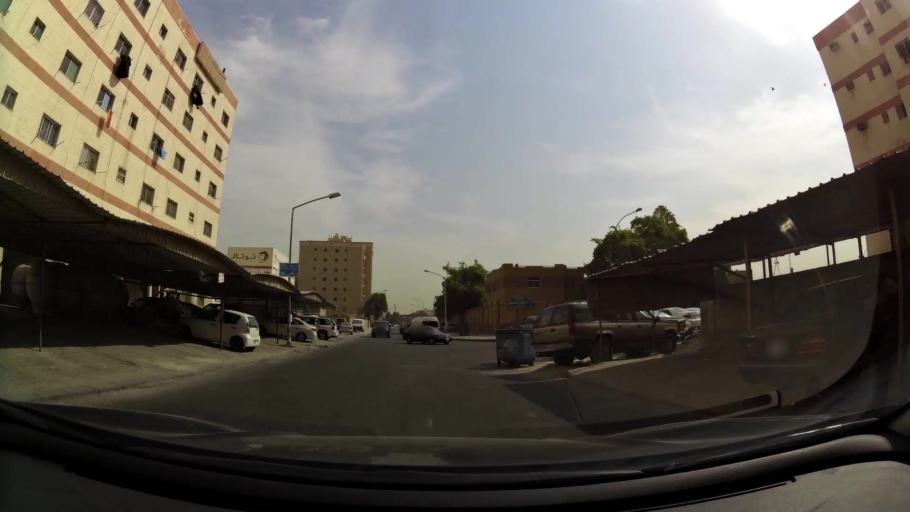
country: KW
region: Al Farwaniyah
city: Janub as Surrah
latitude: 29.2806
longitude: 47.9744
